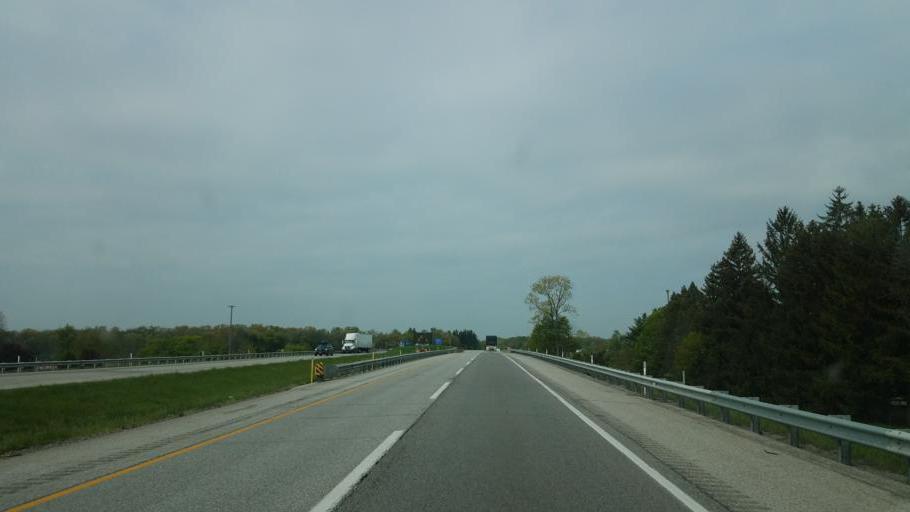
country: US
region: Indiana
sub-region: Elkhart County
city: Bristol
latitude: 41.7332
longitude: -85.8401
